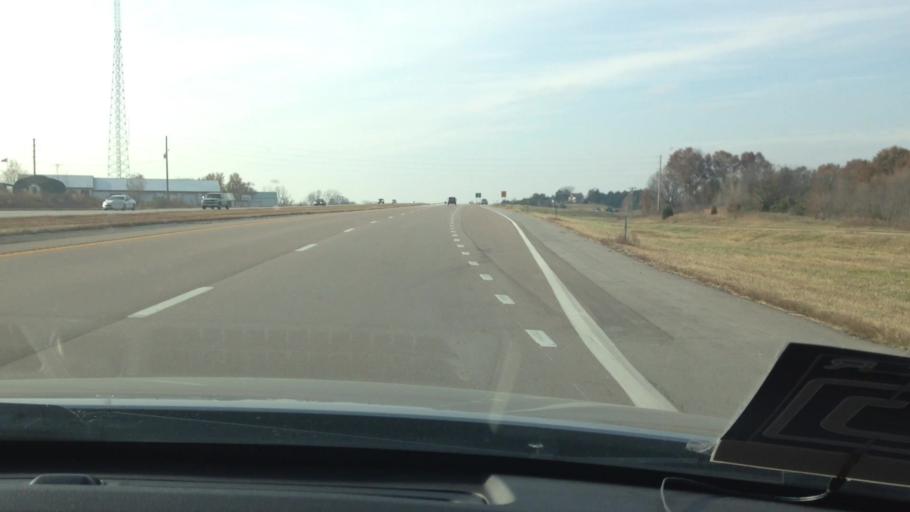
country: US
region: Missouri
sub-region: Cass County
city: Garden City
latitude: 38.4647
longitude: -93.9959
